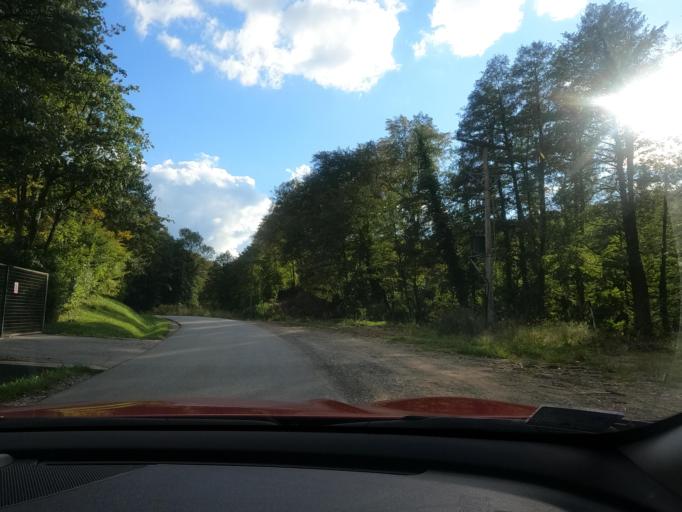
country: HR
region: Sisacko-Moslavacka
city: Petrinja
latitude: 45.3969
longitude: 16.2443
